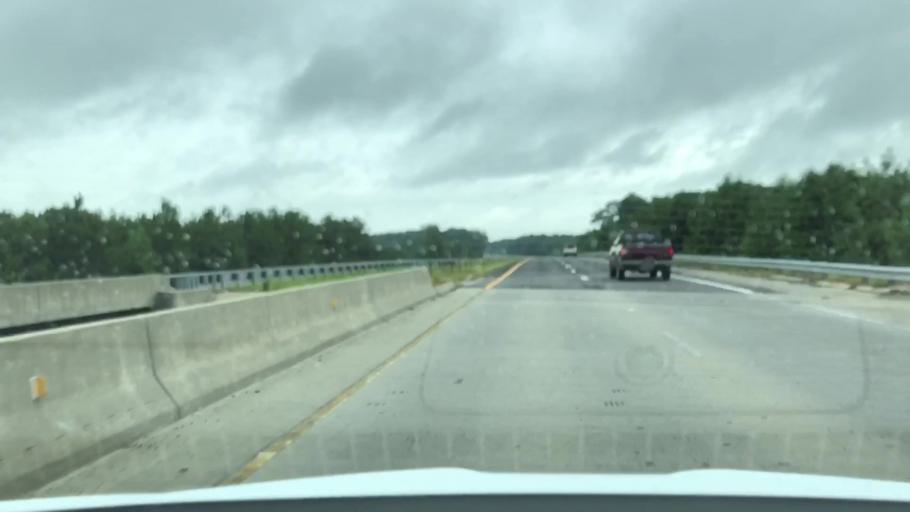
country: US
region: North Carolina
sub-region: Wayne County
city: Fremont
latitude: 35.4691
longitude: -77.9865
